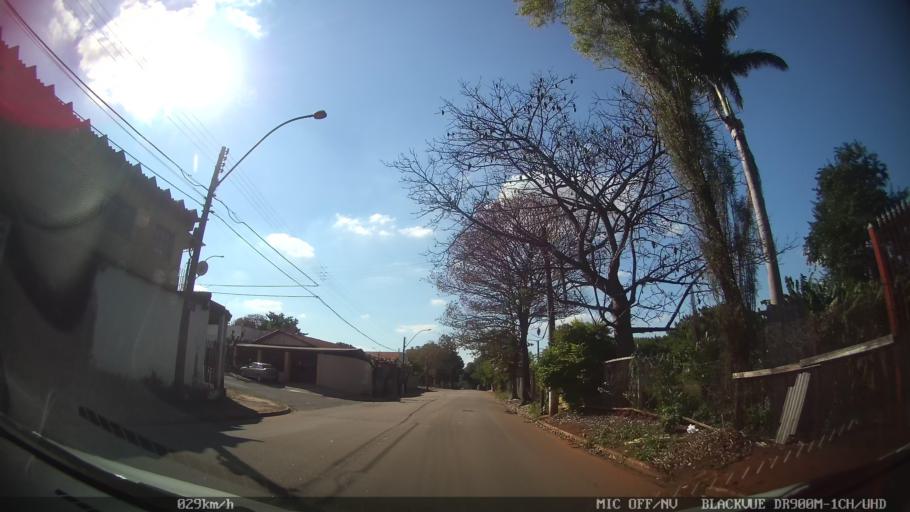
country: BR
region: Sao Paulo
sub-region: Sumare
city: Sumare
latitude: -22.8169
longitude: -47.2798
